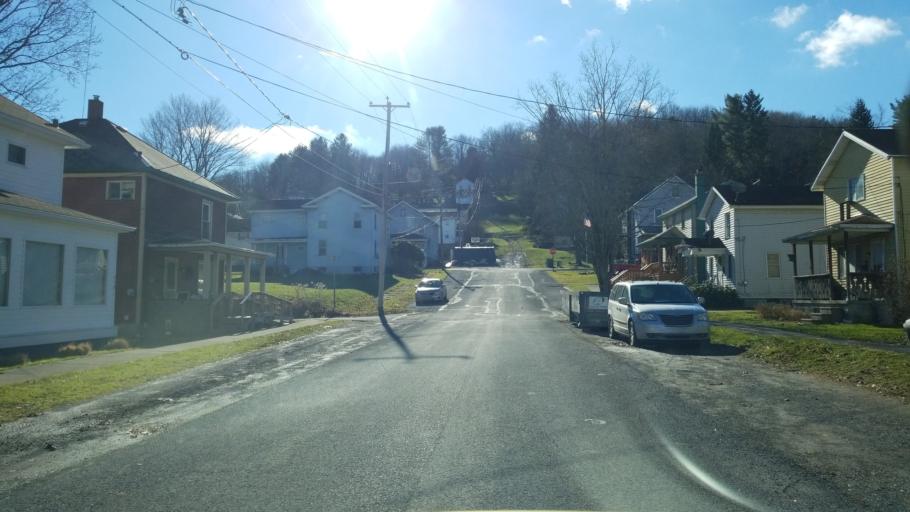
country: US
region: Pennsylvania
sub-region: Jefferson County
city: Brockway
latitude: 41.2487
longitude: -78.7997
